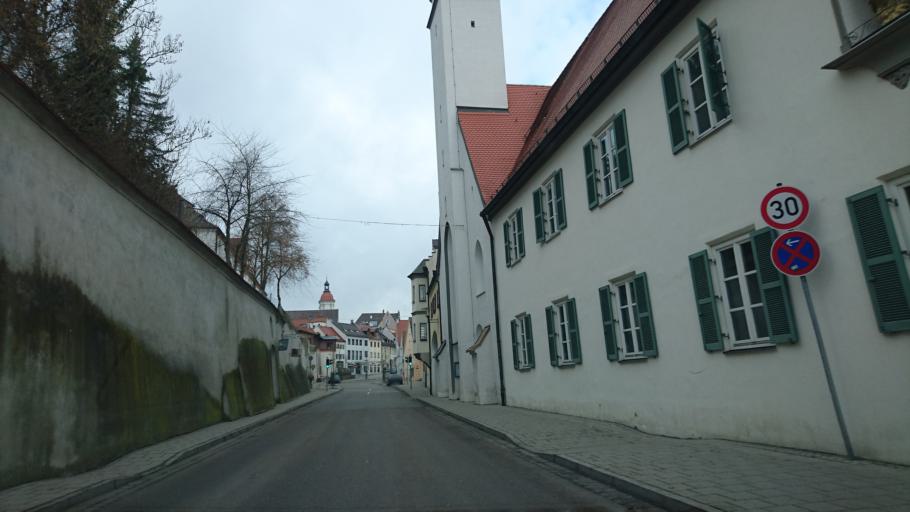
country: DE
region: Bavaria
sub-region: Swabia
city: Dillingen an der Donau
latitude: 48.5757
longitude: 10.4970
